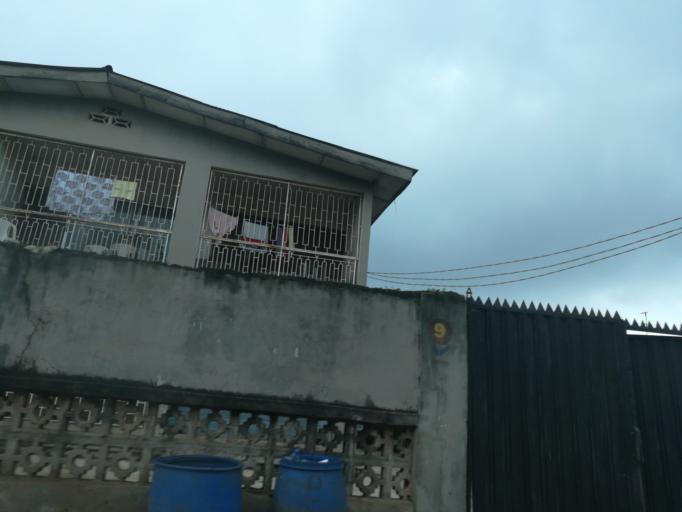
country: NG
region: Lagos
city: Agege
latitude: 6.6121
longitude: 3.3260
